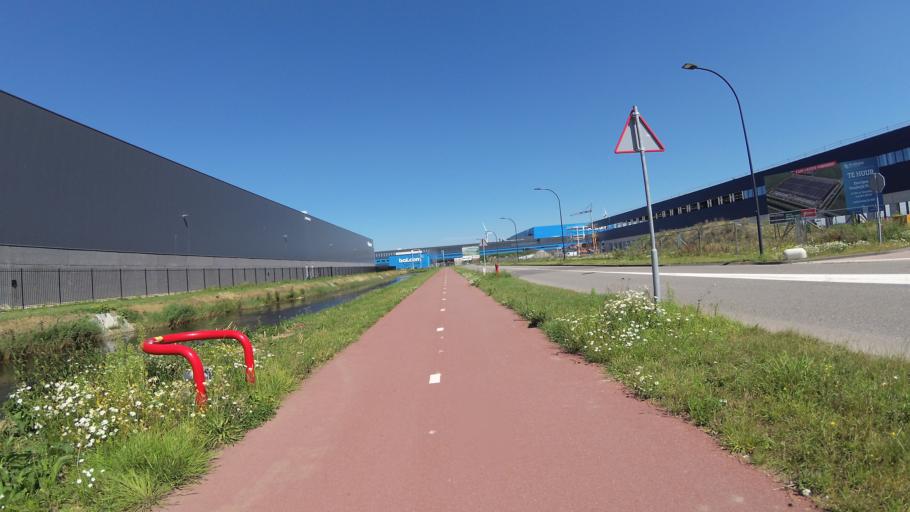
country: NL
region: North Brabant
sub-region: Gemeente Waalwijk
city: Waalwijk
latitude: 51.6997
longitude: 5.0684
